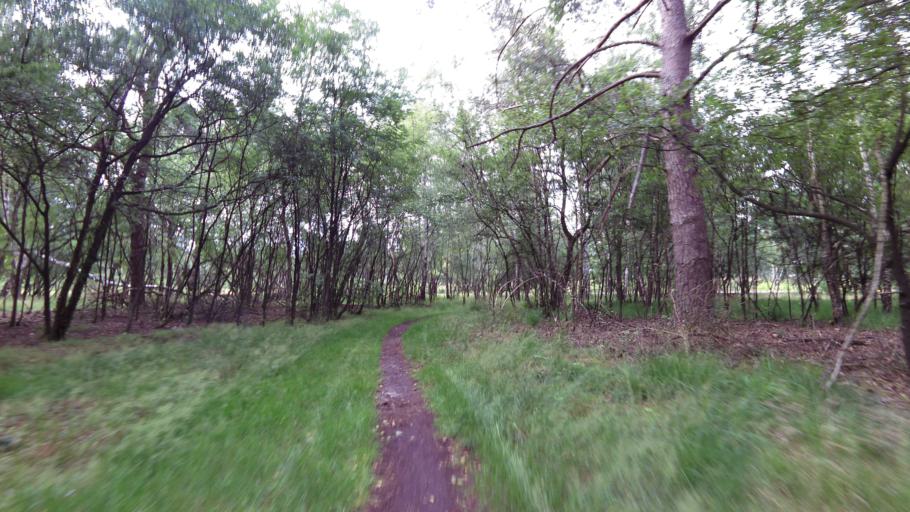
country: NL
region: Gelderland
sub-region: Gemeente Apeldoorn
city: Uddel
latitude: 52.2005
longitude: 5.8449
